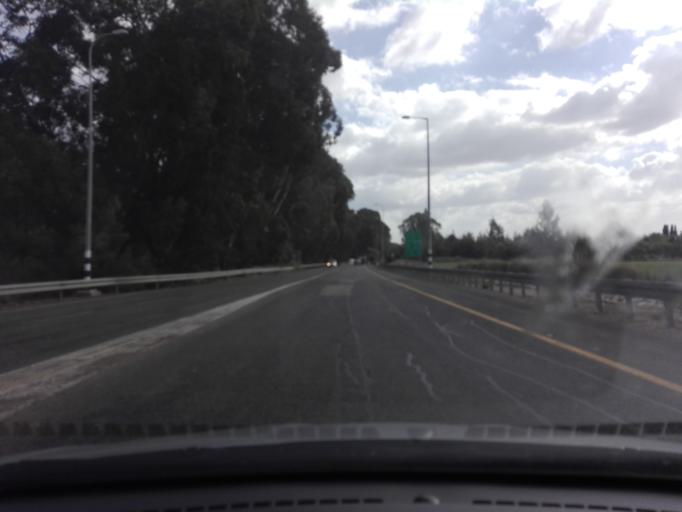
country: PS
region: West Bank
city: Nazlat `Isa
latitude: 32.4642
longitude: 34.9950
